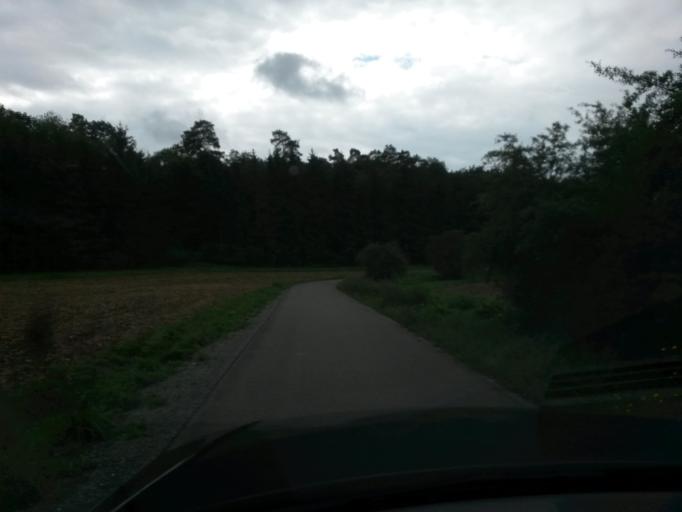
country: DE
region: Bavaria
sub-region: Regierungsbezirk Unterfranken
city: Gadheim
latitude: 49.8471
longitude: 9.9217
